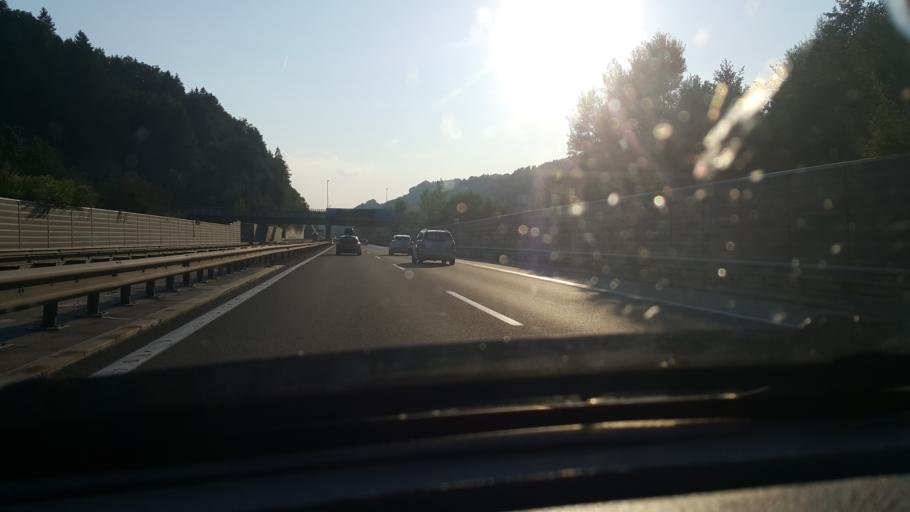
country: SI
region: Moravce
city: Moravce
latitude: 46.1737
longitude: 14.7898
